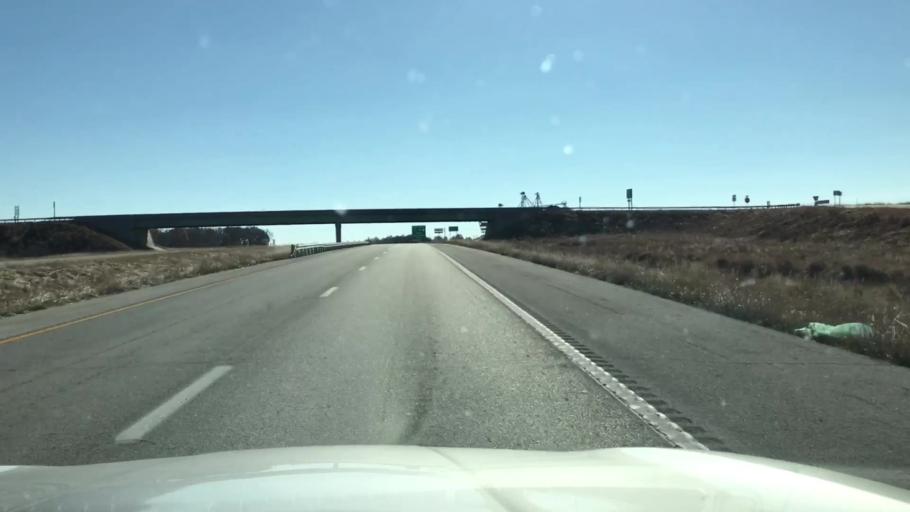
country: US
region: Missouri
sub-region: Jasper County
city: Carthage
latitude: 37.0980
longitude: -94.3119
